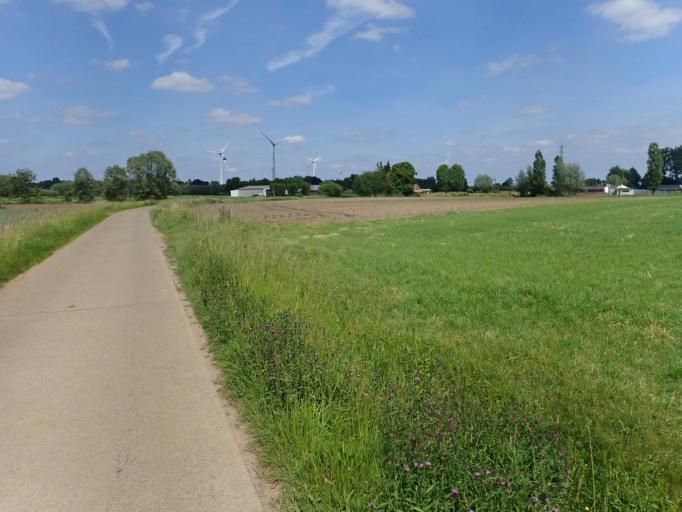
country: BE
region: Flanders
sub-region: Provincie Antwerpen
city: Willebroek
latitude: 51.0694
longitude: 4.3307
